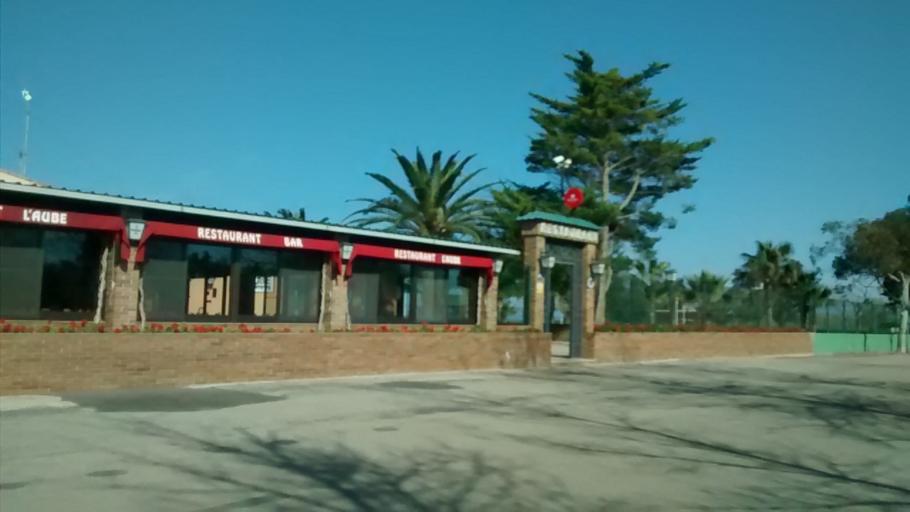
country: ES
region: Catalonia
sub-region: Provincia de Tarragona
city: Deltebre
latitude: 40.7195
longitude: 0.8494
